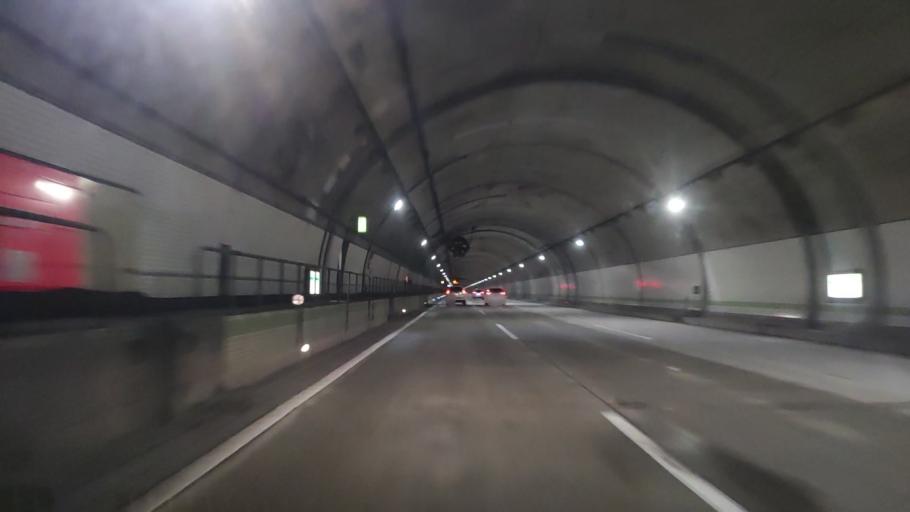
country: JP
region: Hyogo
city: Akashi
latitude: 34.6517
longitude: 135.0604
